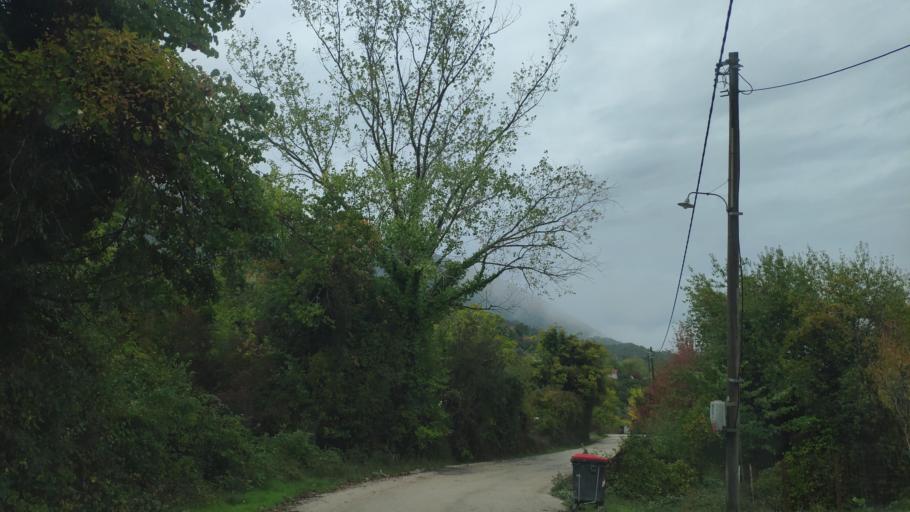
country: GR
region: Epirus
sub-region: Nomos Thesprotias
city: Paramythia
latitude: 39.4627
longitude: 20.6736
